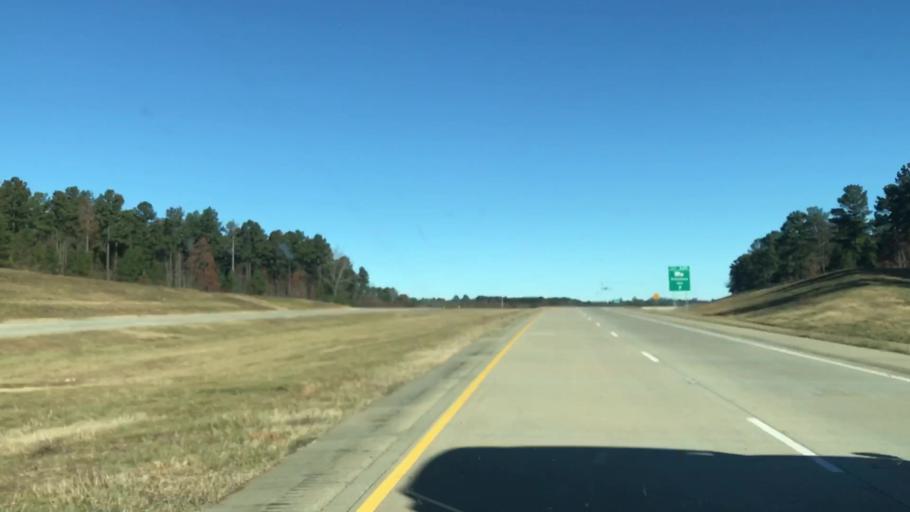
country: US
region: Louisiana
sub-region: Caddo Parish
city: Vivian
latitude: 32.9898
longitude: -93.9104
